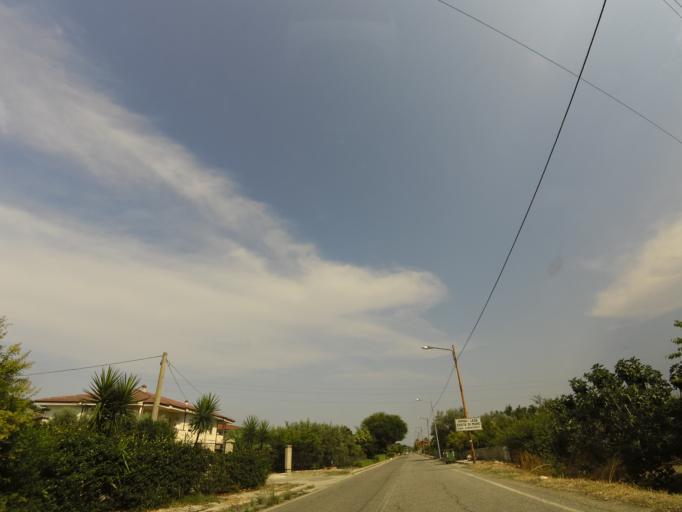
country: IT
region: Calabria
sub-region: Provincia di Reggio Calabria
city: Monasterace
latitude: 38.4456
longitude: 16.5358
